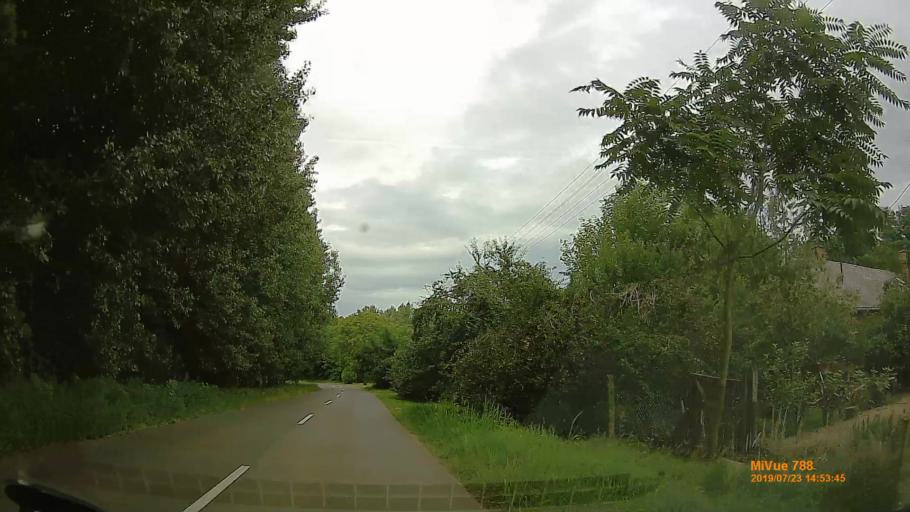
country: HU
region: Szabolcs-Szatmar-Bereg
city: Kalmanhaza
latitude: 47.8806
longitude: 21.6522
